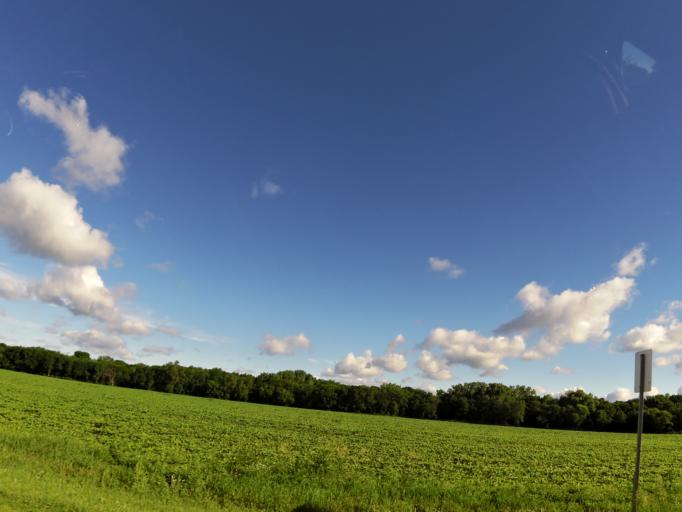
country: US
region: Minnesota
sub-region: Dakota County
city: Hastings
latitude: 44.7170
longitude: -92.8719
